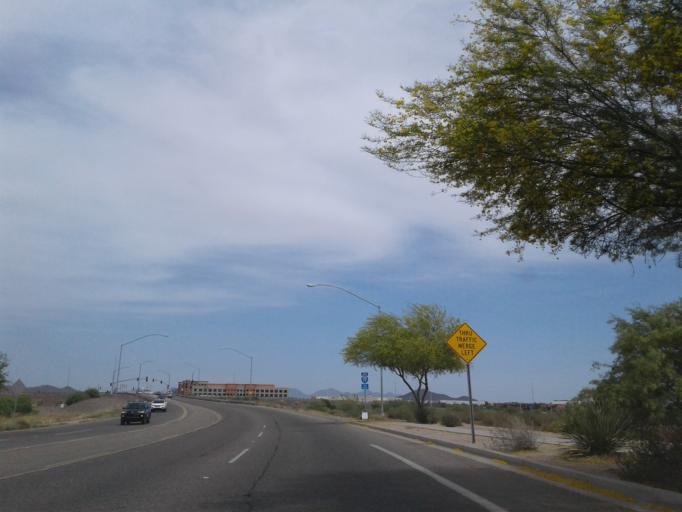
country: US
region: Arizona
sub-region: Maricopa County
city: Peoria
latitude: 33.6994
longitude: -112.1191
